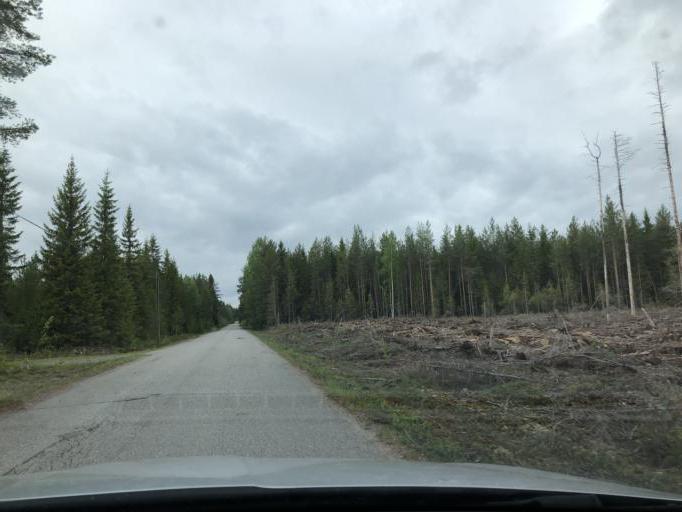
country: SE
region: Norrbotten
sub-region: Pitea Kommun
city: Roknas
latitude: 65.3792
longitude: 21.2760
